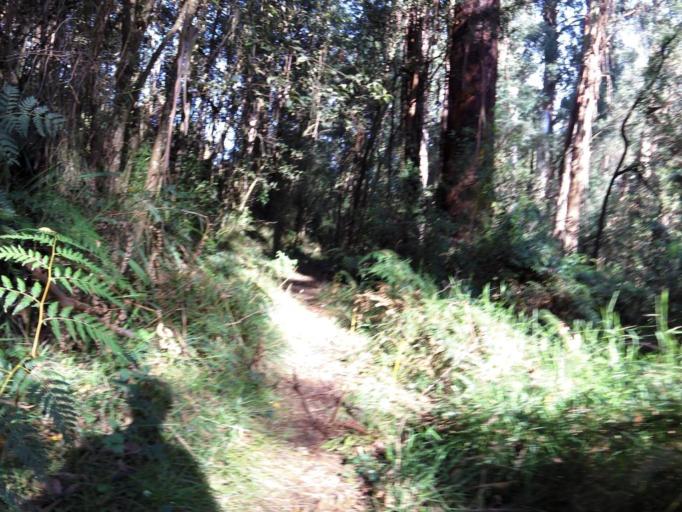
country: AU
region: Victoria
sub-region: Yarra Ranges
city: Monbulk
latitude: -37.8757
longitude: 145.4030
